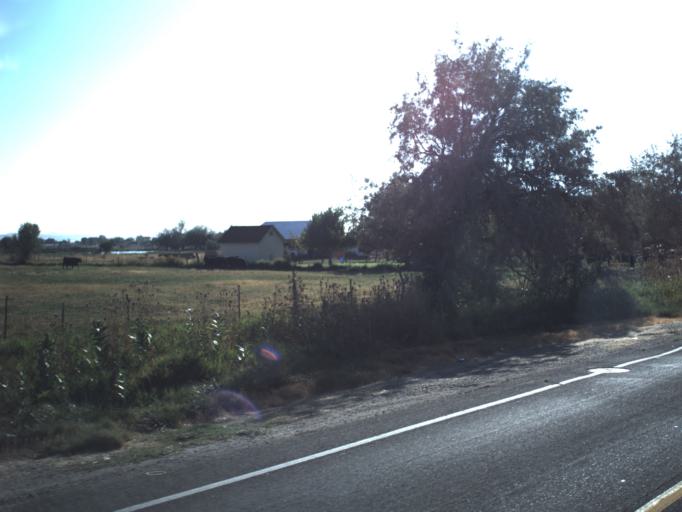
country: US
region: Utah
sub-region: Davis County
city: West Point
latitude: 41.1399
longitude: -112.1023
